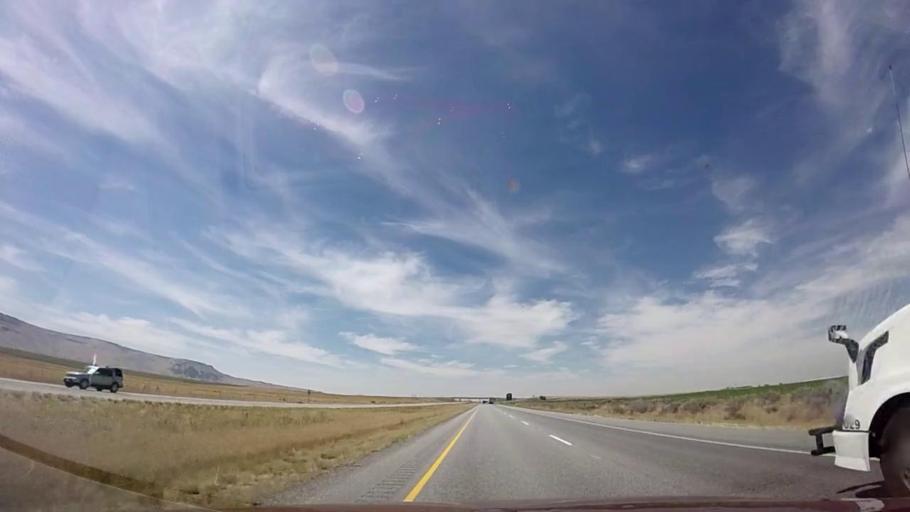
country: US
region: Idaho
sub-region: Minidoka County
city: Rupert
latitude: 42.5116
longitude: -113.4163
